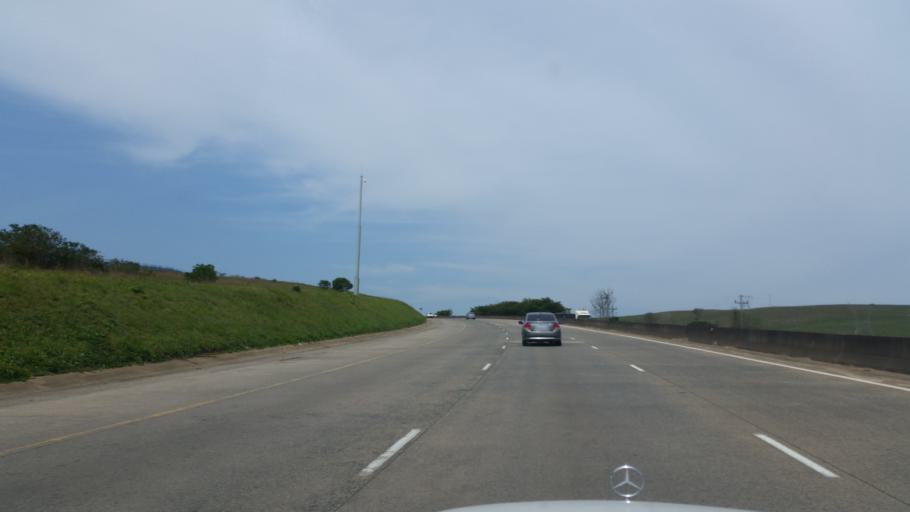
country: ZA
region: KwaZulu-Natal
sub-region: eThekwini Metropolitan Municipality
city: Mpumalanga
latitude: -29.7422
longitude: 30.6279
